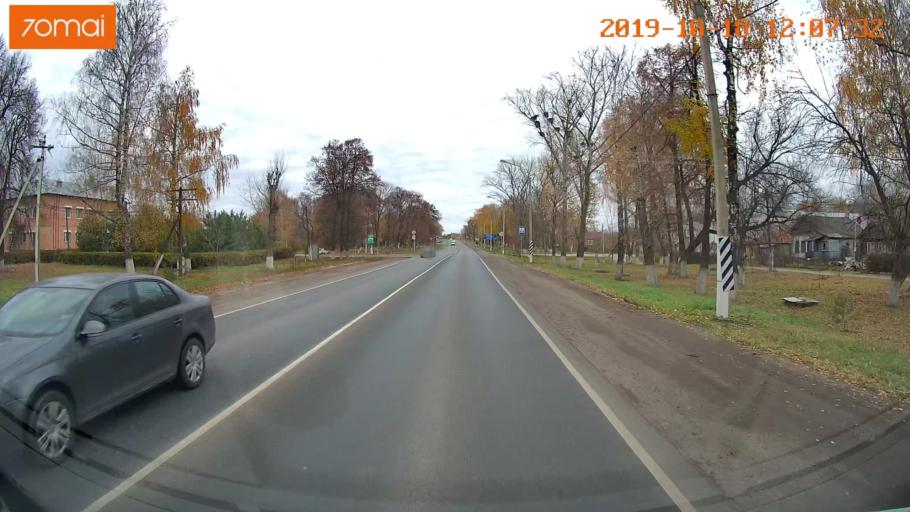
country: RU
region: Rjazan
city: Zakharovo
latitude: 54.3699
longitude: 39.2814
